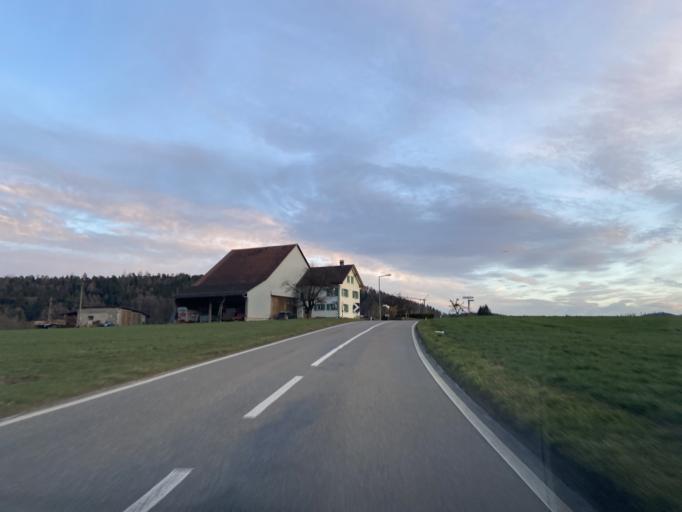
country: CH
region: Zurich
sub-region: Bezirk Winterthur
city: Wuelflingen (Kreis 6) / Lindenplatz
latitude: 47.5255
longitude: 8.6953
